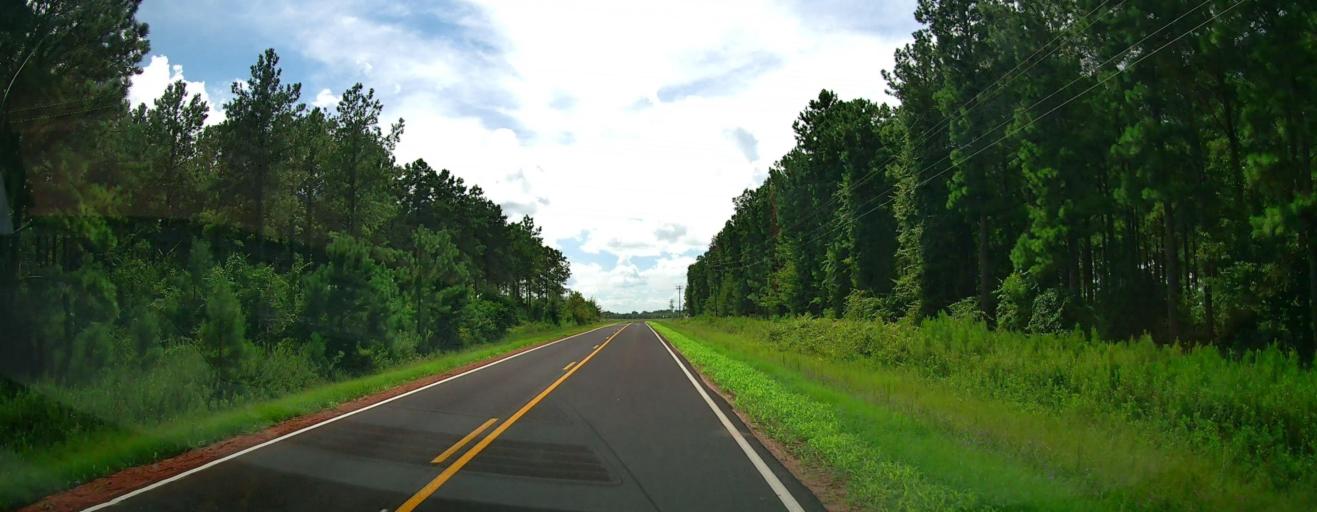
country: US
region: Georgia
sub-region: Macon County
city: Marshallville
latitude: 32.4666
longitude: -83.9018
